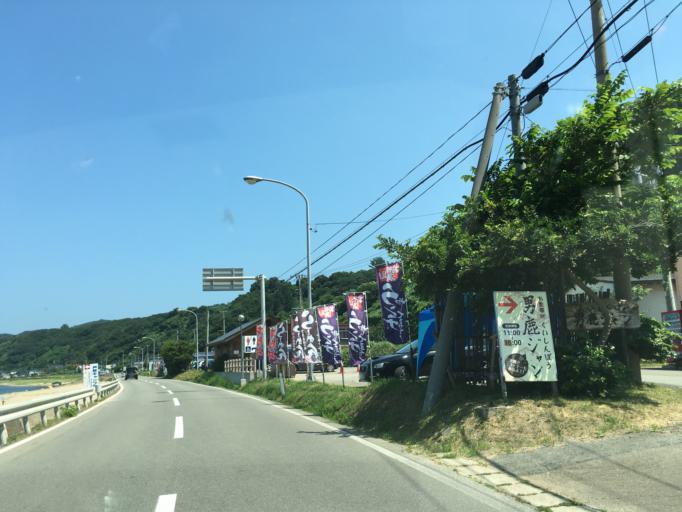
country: JP
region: Akita
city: Tenno
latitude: 39.9464
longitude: 139.7198
